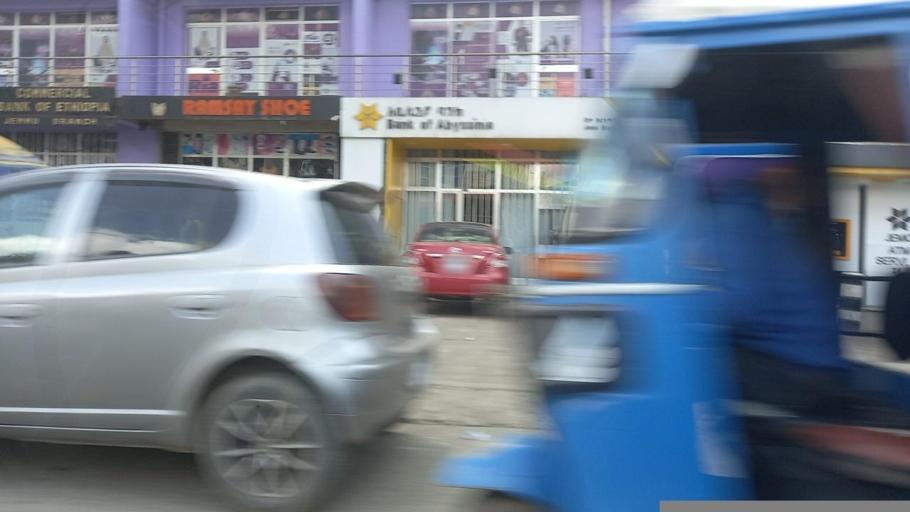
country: ET
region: Adis Abeba
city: Addis Ababa
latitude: 8.9609
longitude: 38.7142
